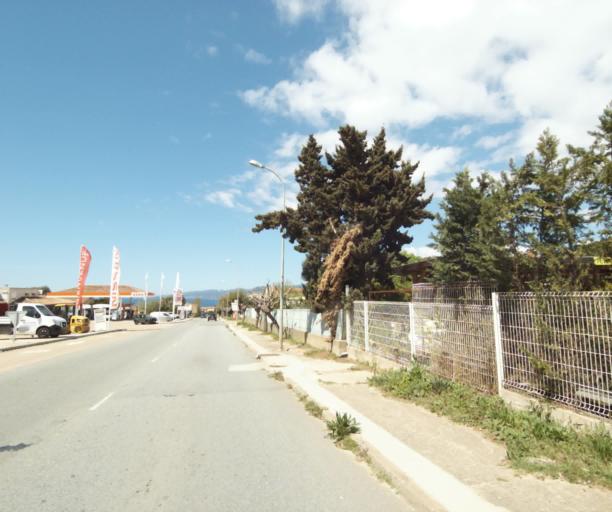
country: FR
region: Corsica
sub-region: Departement de la Corse-du-Sud
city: Propriano
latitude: 41.6703
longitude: 8.9143
